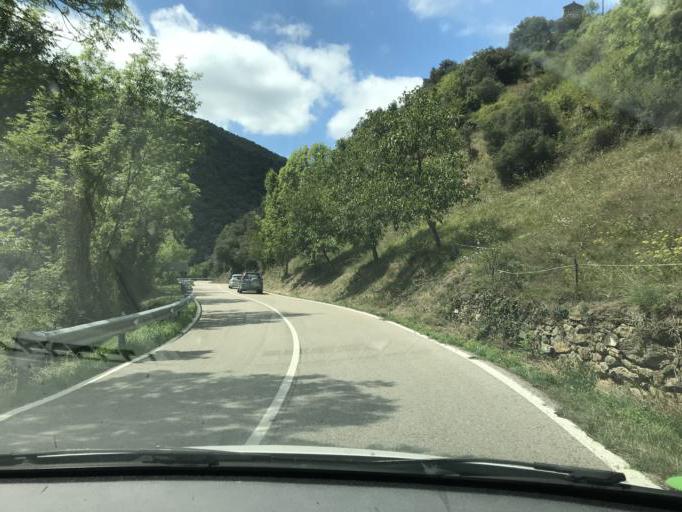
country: ES
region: Cantabria
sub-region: Provincia de Cantabria
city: Cabezon de Liebana
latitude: 43.0759
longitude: -4.5392
